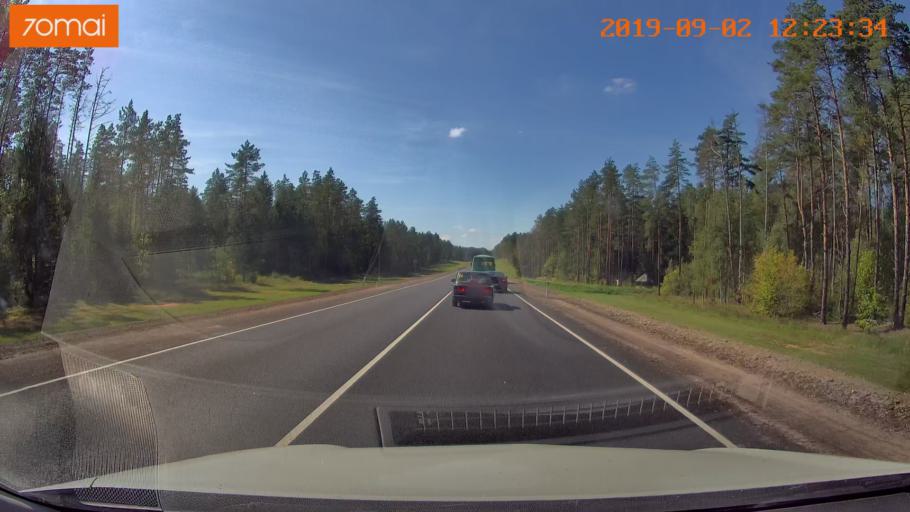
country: RU
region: Smolensk
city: Shumyachi
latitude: 53.8736
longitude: 32.6186
